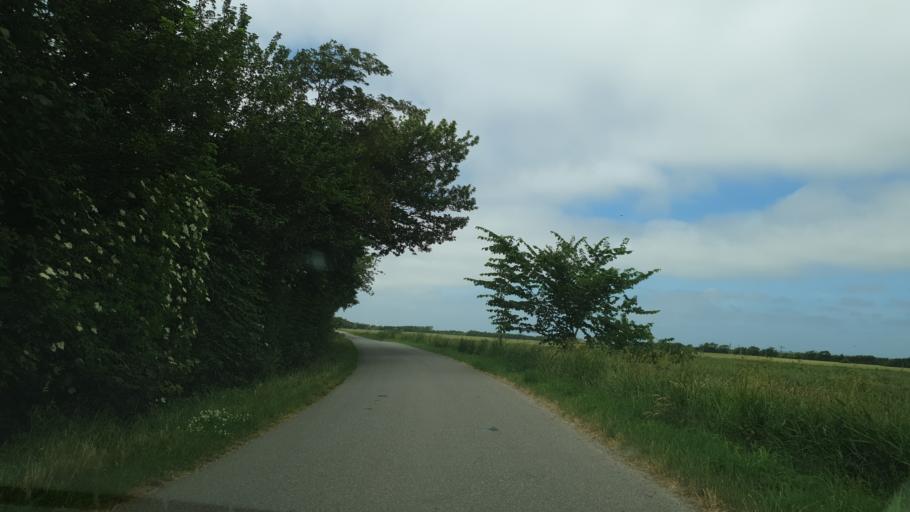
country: DK
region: Central Jutland
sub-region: Ringkobing-Skjern Kommune
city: Skjern
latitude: 55.9337
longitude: 8.4024
